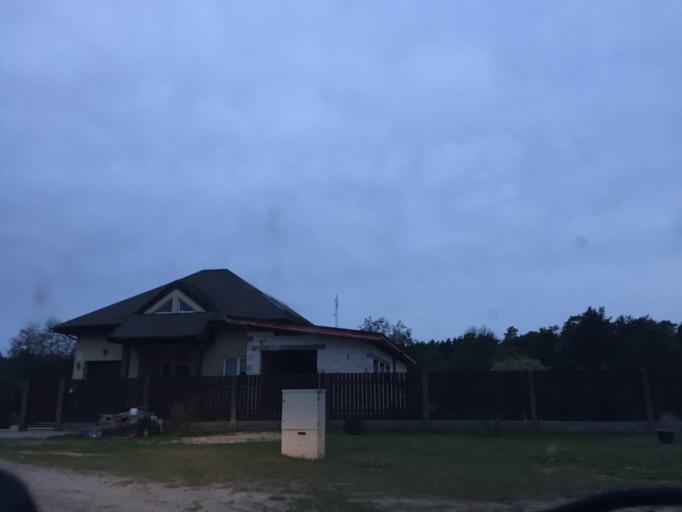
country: LV
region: Adazi
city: Adazi
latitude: 57.0896
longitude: 24.3743
